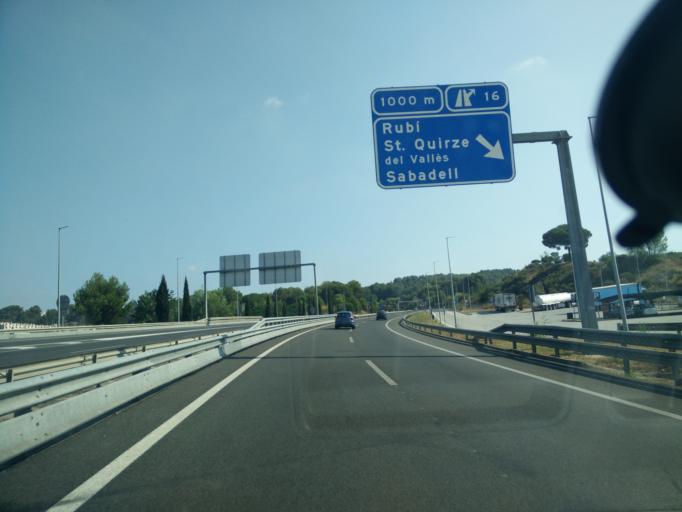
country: ES
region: Catalonia
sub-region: Provincia de Barcelona
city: Rubi
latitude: 41.4983
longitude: 2.0489
